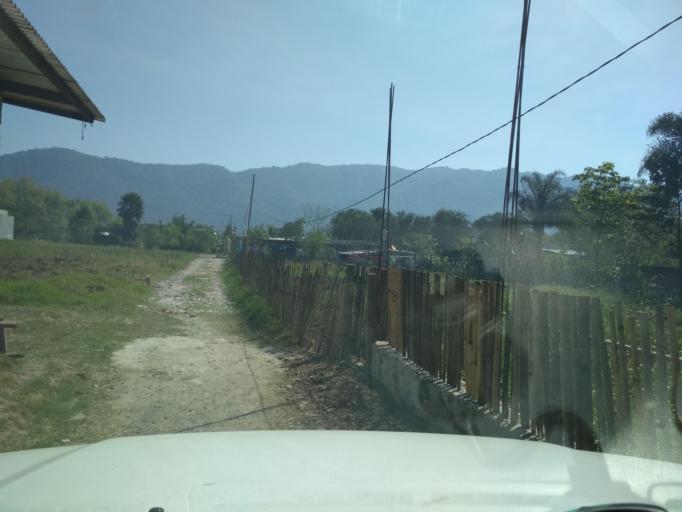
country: MX
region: Veracruz
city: Jalapilla
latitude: 18.8172
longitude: -97.0875
